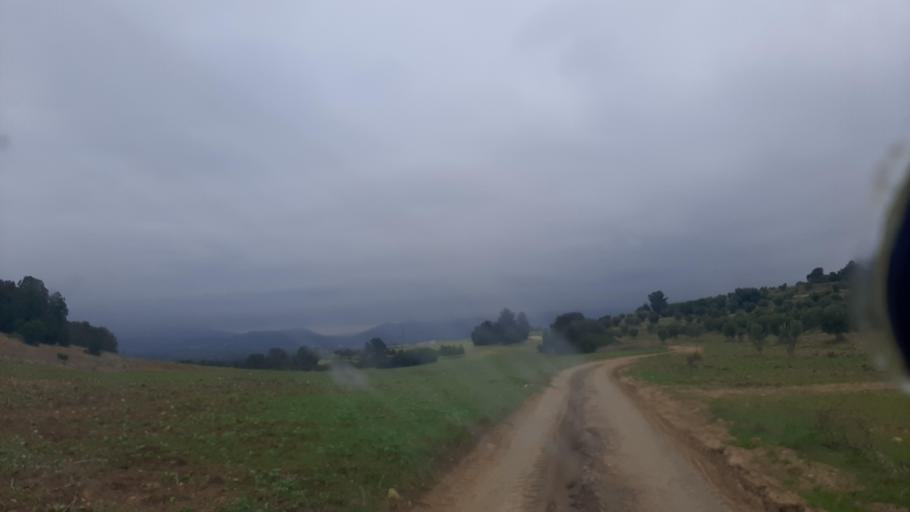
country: TN
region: Tunis
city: La Sebala du Mornag
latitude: 36.5764
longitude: 10.2916
